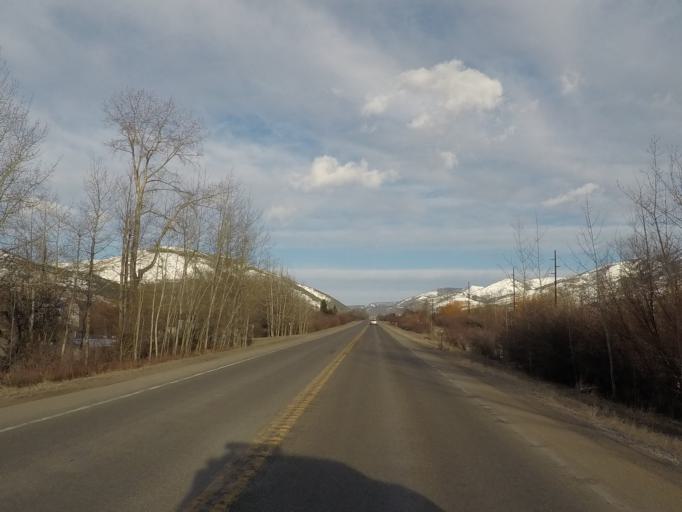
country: US
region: Montana
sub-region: Deer Lodge County
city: Anaconda
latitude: 46.1429
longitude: -112.9938
